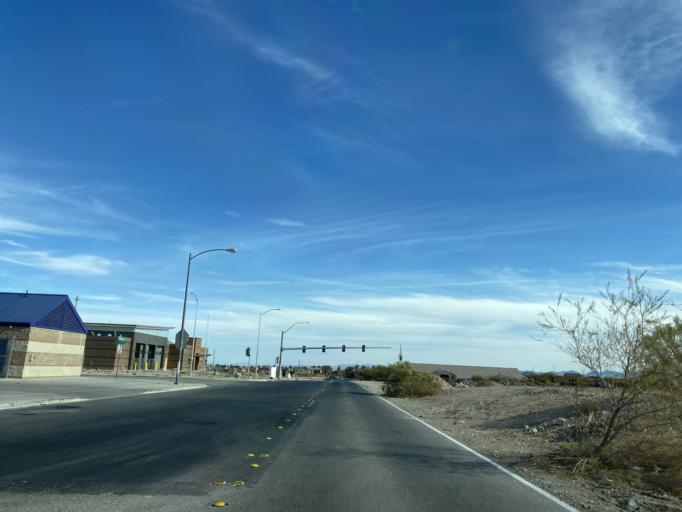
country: US
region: Nevada
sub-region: Clark County
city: Enterprise
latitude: 36.0483
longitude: -115.2663
